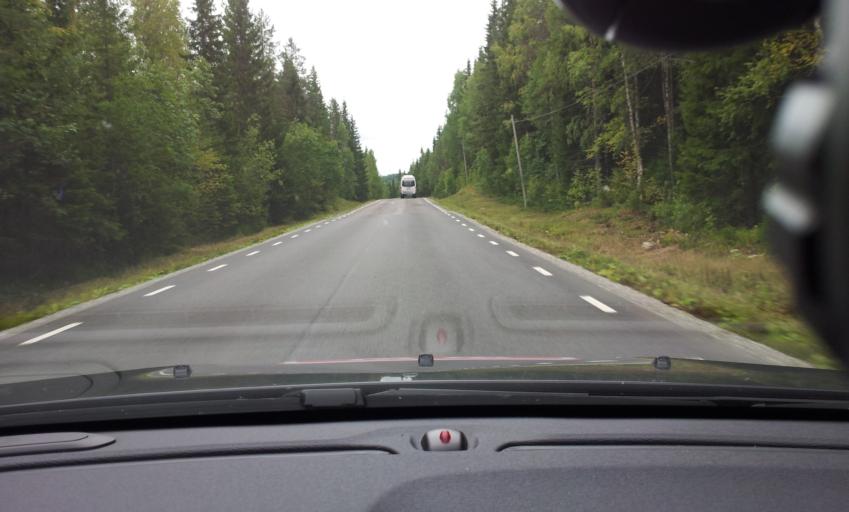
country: SE
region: Jaemtland
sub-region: Braecke Kommun
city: Braecke
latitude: 63.0084
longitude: 15.1985
